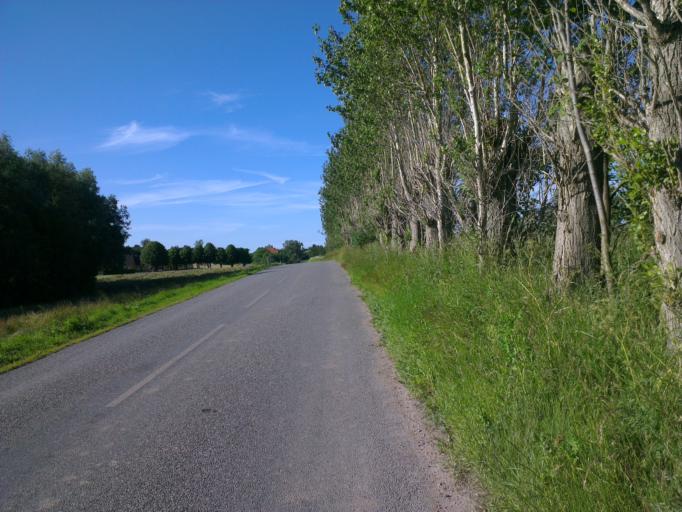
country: DK
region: Capital Region
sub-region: Frederikssund Kommune
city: Skibby
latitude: 55.7454
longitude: 12.0342
